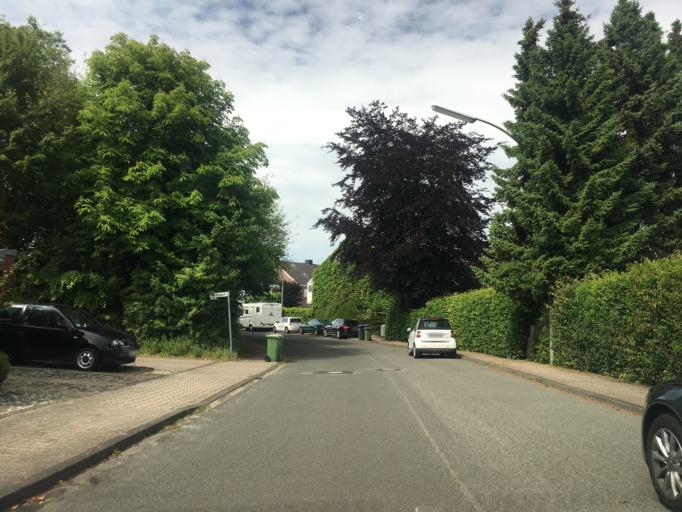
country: DE
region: North Rhine-Westphalia
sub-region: Regierungsbezirk Munster
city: Altenberge
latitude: 52.0533
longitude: 7.4732
